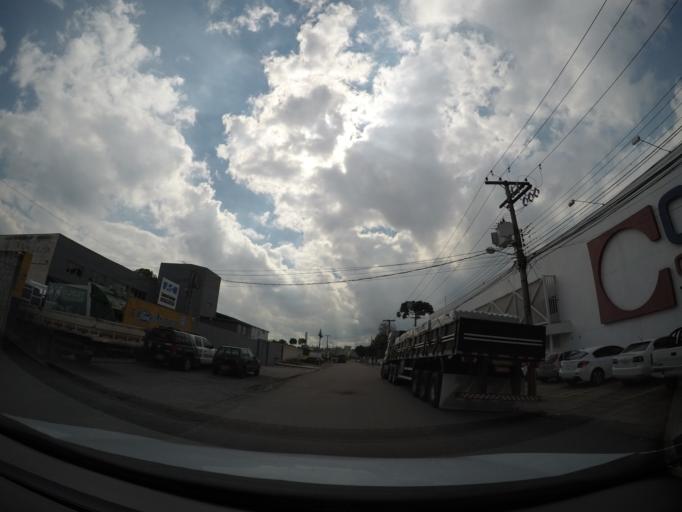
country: BR
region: Parana
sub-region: Curitiba
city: Curitiba
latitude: -25.4737
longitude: -49.2550
